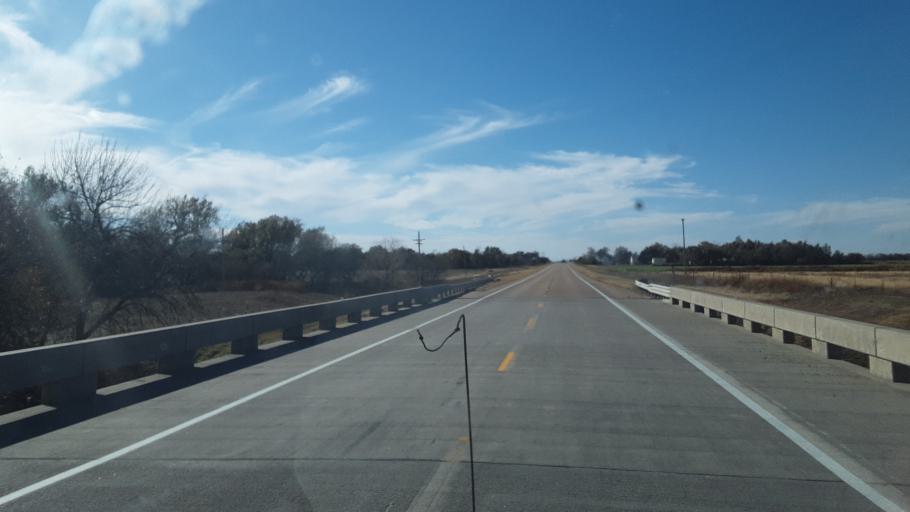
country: US
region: Kansas
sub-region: Pawnee County
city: Larned
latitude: 38.1897
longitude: -99.3229
